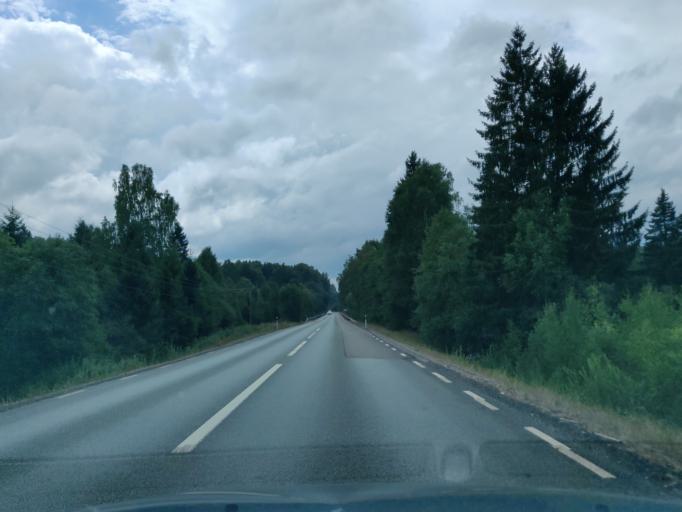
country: SE
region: Vaermland
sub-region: Munkfors Kommun
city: Munkfors
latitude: 59.9130
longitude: 13.5702
